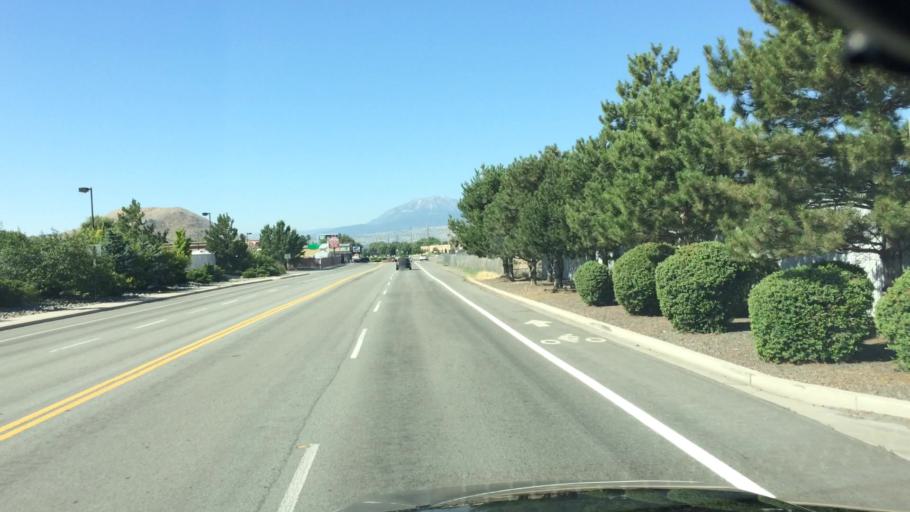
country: US
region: Nevada
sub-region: Washoe County
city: Sparks
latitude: 39.4976
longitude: -119.7527
